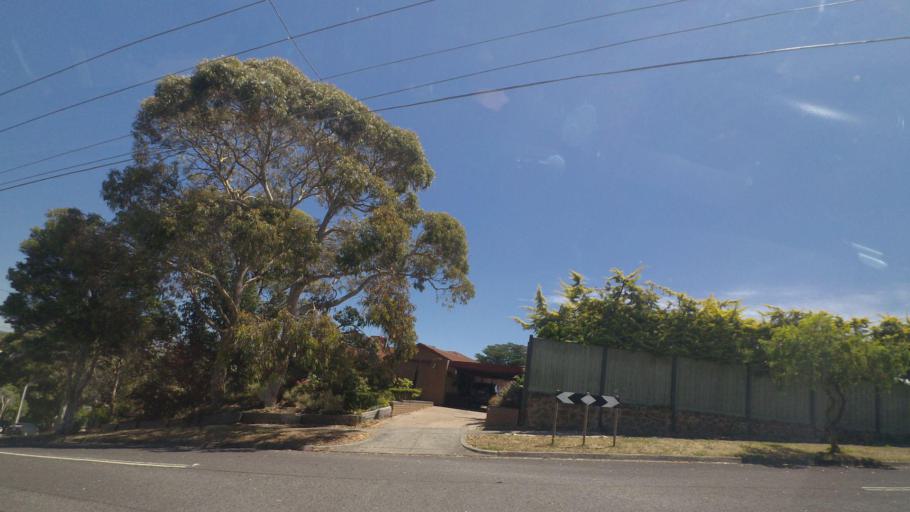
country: AU
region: Victoria
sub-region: Maroondah
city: Croydon North
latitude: -37.7802
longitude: 145.3196
